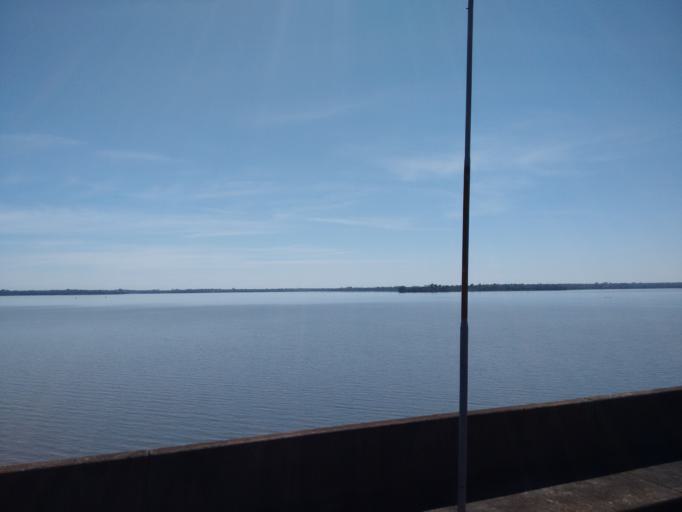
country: PY
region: Alto Parana
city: Ciudad del Este
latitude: -25.4253
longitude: -54.5655
